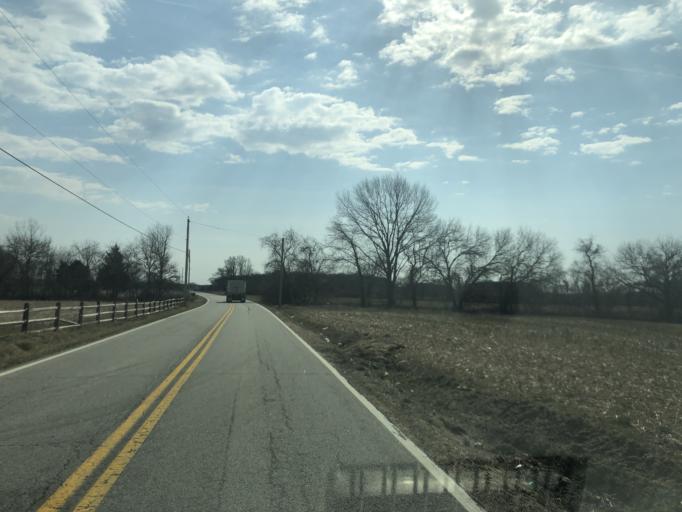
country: US
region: Maryland
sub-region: Queen Anne's County
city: Centreville
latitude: 39.0905
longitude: -75.9487
